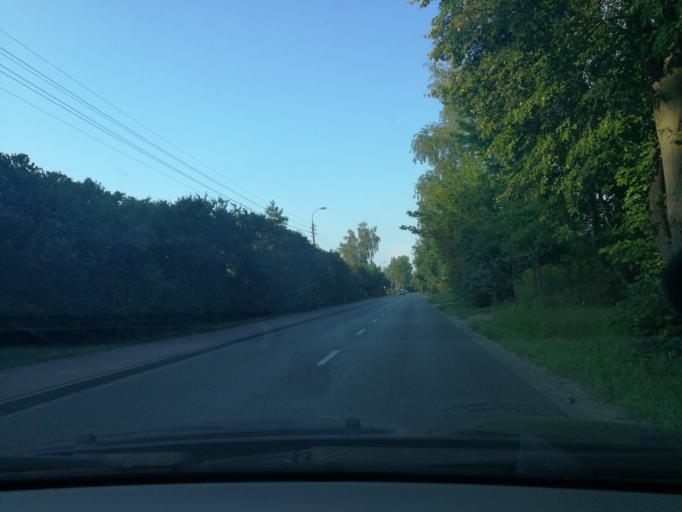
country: PL
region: Masovian Voivodeship
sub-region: Powiat pruszkowski
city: Brwinow
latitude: 52.1511
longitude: 20.7275
